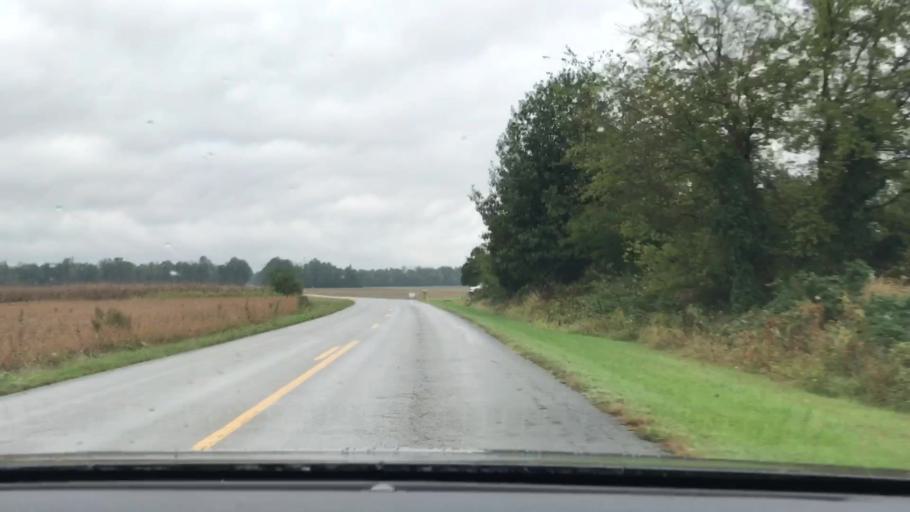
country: US
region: Kentucky
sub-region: McLean County
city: Calhoun
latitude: 37.3976
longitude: -87.2820
